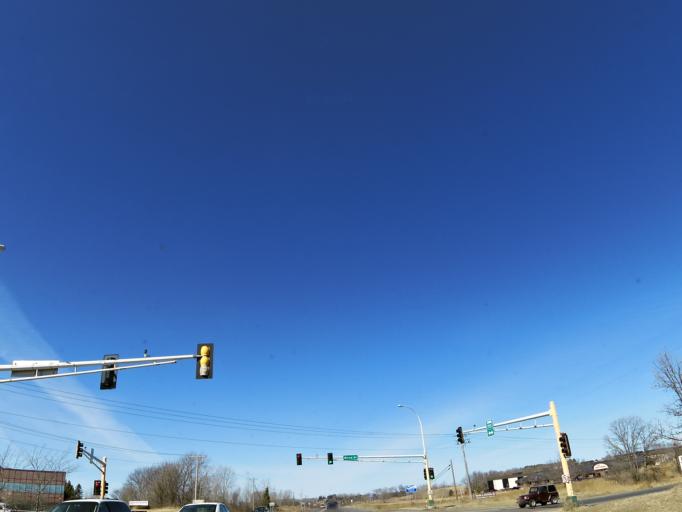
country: US
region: Minnesota
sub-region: Hennepin County
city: Medina
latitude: 45.0580
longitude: -93.5881
